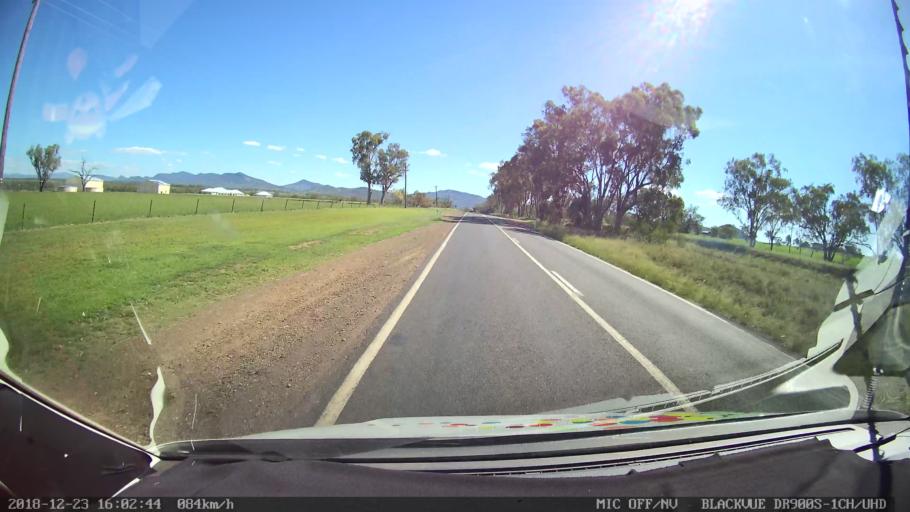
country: AU
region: New South Wales
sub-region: Tamworth Municipality
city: Phillip
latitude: -31.2355
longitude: 150.8066
